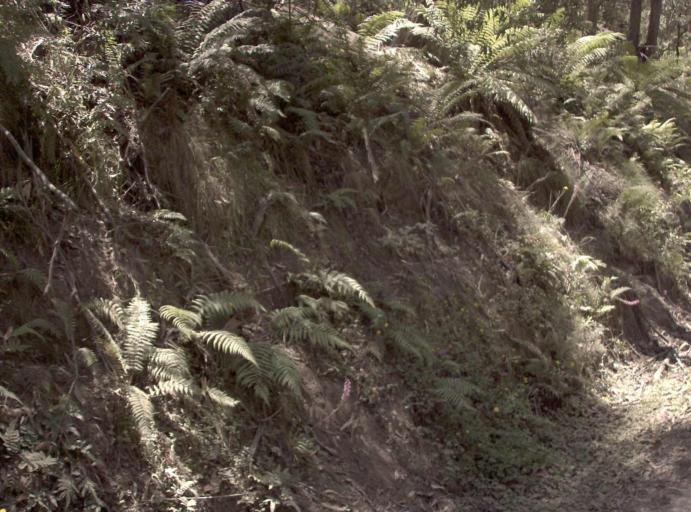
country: AU
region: Victoria
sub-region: Yarra Ranges
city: Millgrove
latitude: -37.5994
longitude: 146.1730
